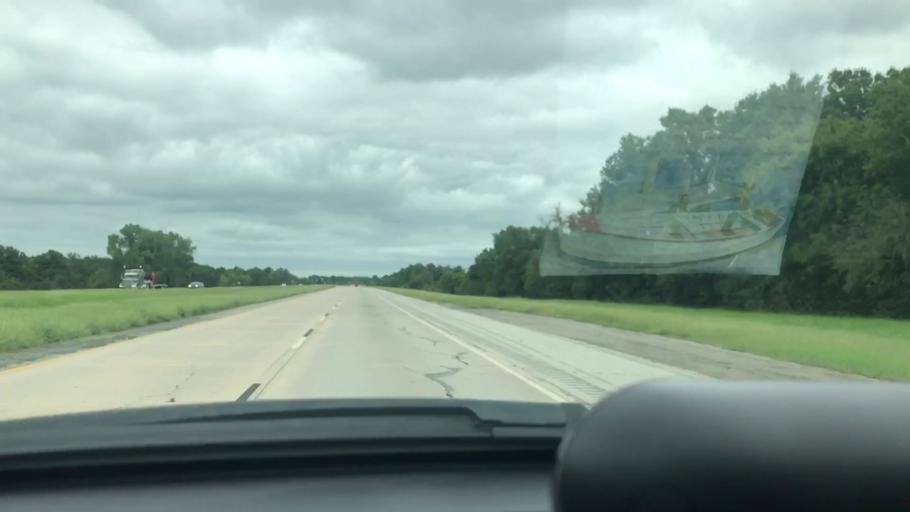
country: US
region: Oklahoma
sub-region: Wagoner County
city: Wagoner
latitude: 35.8974
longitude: -95.4026
